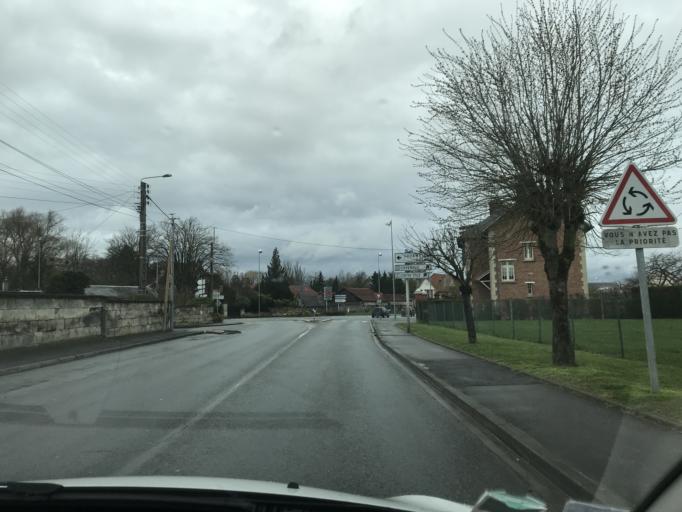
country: FR
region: Picardie
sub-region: Departement de l'Aisne
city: Belleu
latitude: 49.3691
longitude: 3.3308
